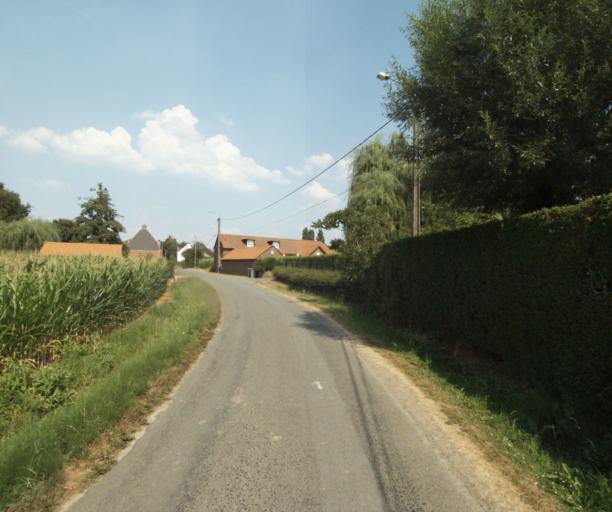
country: FR
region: Nord-Pas-de-Calais
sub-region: Departement du Nord
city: Comines
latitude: 50.7385
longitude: 3.0278
